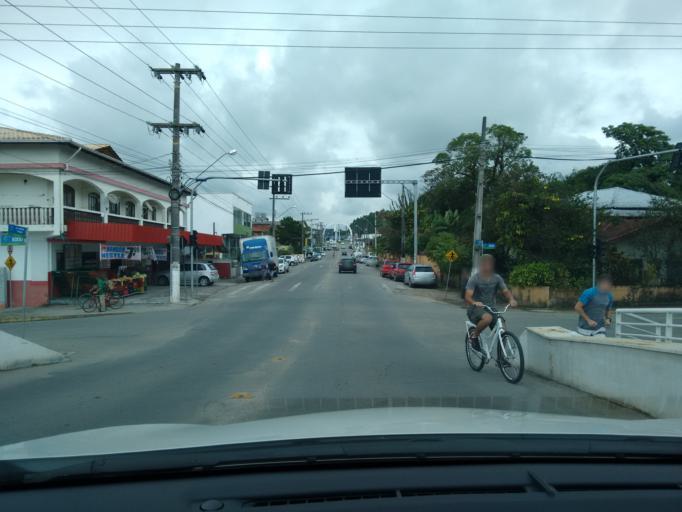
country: BR
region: Santa Catarina
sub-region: Penha
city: Penha
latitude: -26.7612
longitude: -48.6831
